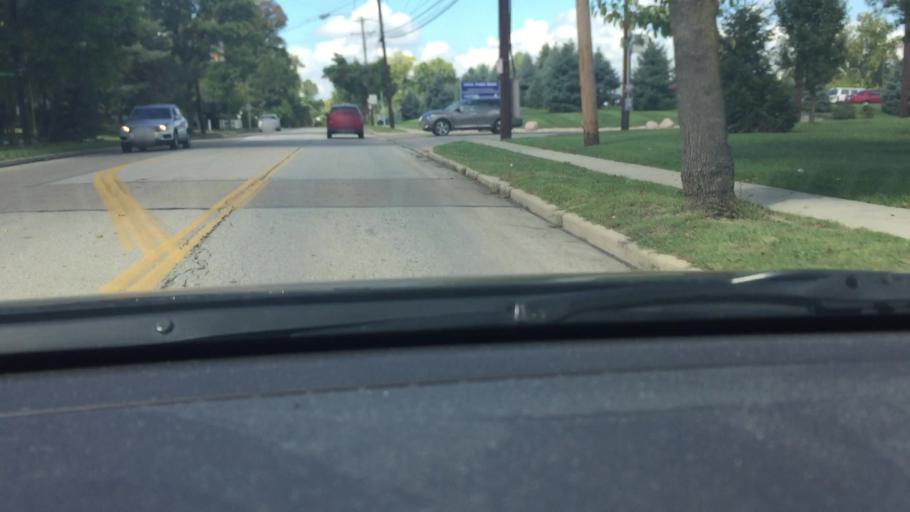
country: US
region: Ohio
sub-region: Hamilton County
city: Fairfax
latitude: 39.1649
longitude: -84.4098
